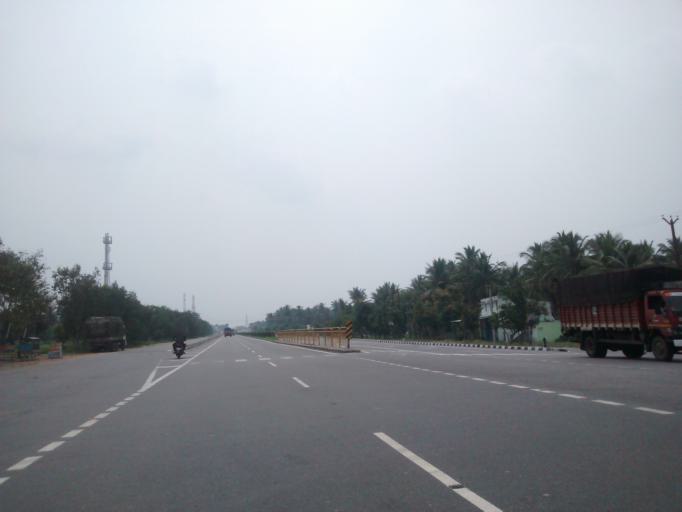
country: IN
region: Tamil Nadu
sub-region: Krishnagiri
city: Kaverippattanam
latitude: 12.3147
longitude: 78.2076
